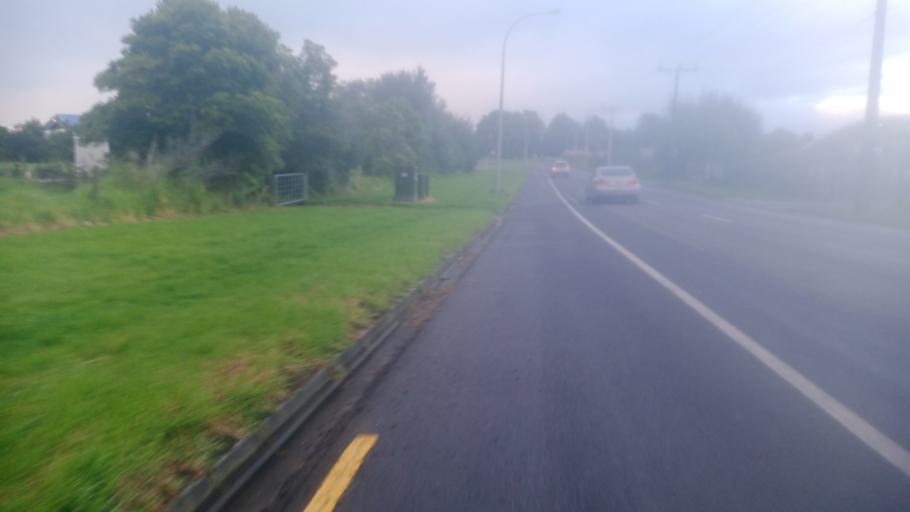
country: NZ
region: Gisborne
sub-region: Gisborne District
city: Gisborne
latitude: -38.6632
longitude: 177.9929
